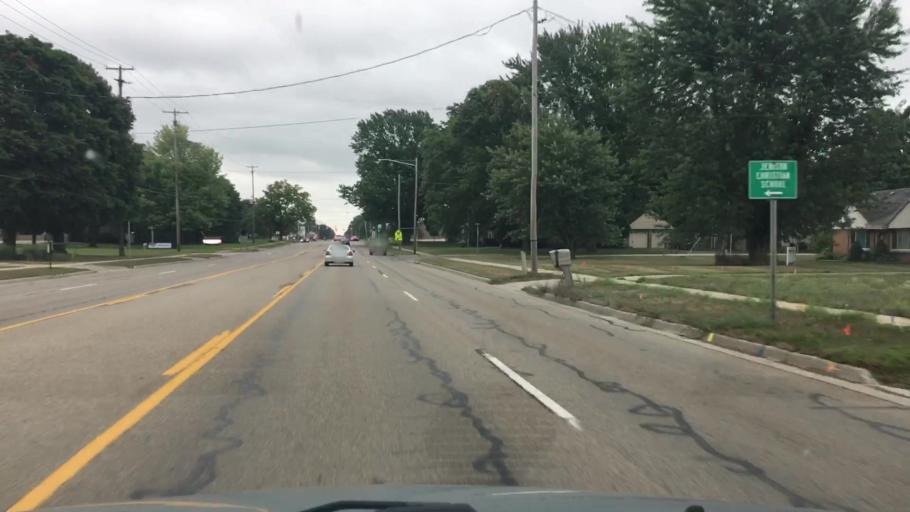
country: US
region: Michigan
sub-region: Ottawa County
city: Jenison
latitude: 42.9071
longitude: -85.8366
